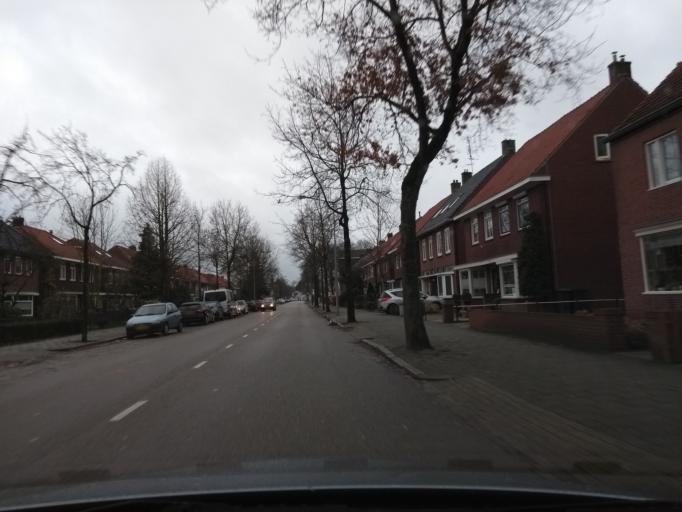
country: NL
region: Overijssel
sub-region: Gemeente Almelo
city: Almelo
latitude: 52.3718
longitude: 6.6667
